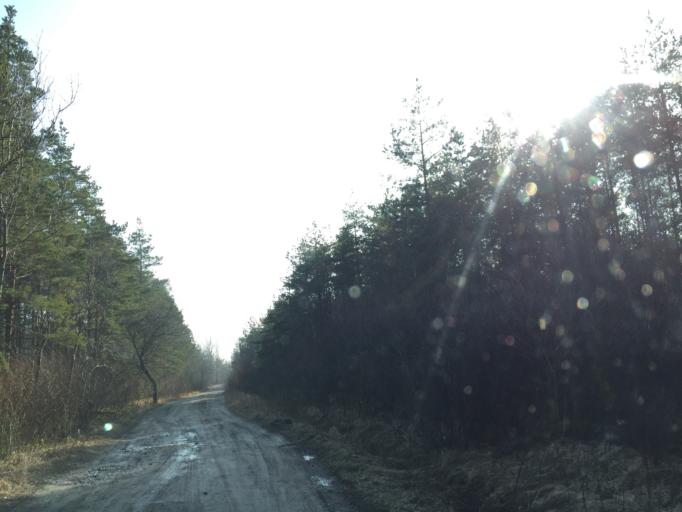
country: EE
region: Saare
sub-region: Kuressaare linn
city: Kuressaare
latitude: 58.2372
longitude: 22.4469
